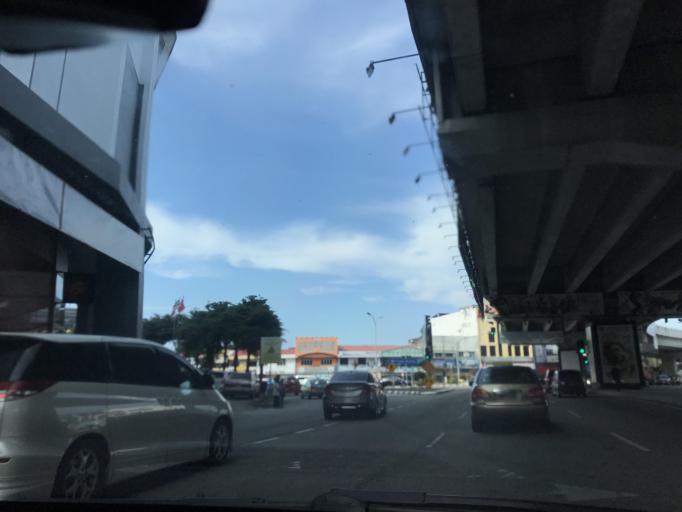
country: MY
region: Kelantan
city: Kota Bharu
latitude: 6.1171
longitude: 102.2414
